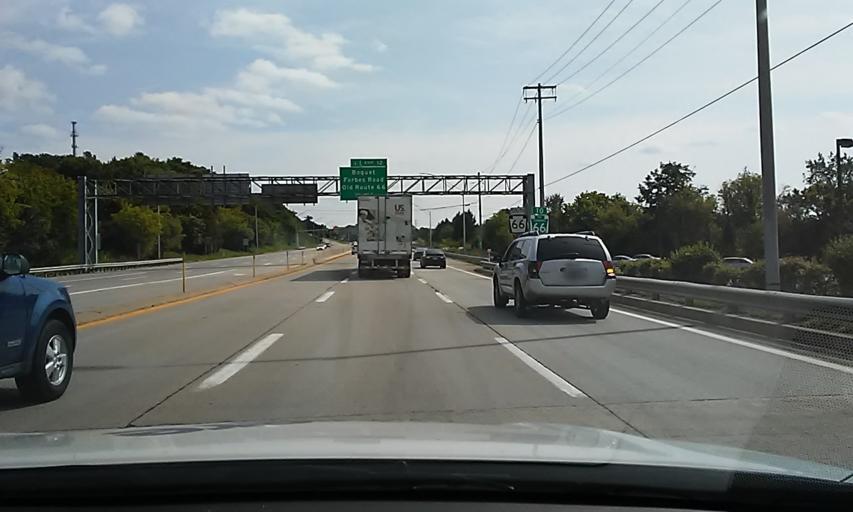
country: US
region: Pennsylvania
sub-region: Westmoreland County
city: Delmont
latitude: 40.3950
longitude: -79.5710
